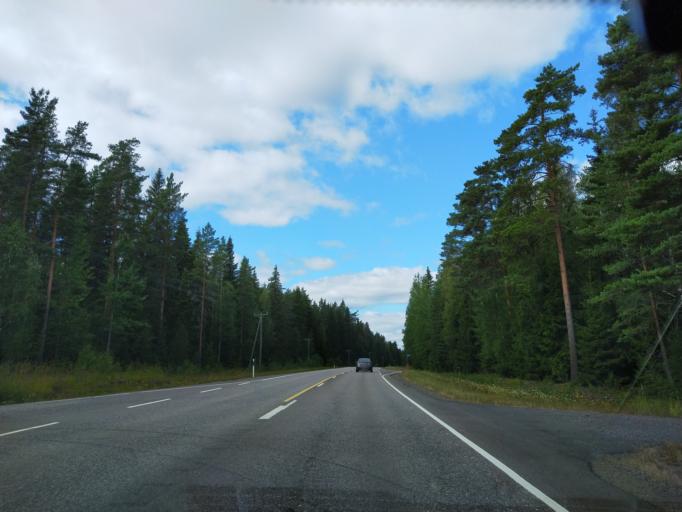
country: FI
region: Haeme
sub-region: Riihimaeki
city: Loppi
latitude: 60.7507
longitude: 24.3133
